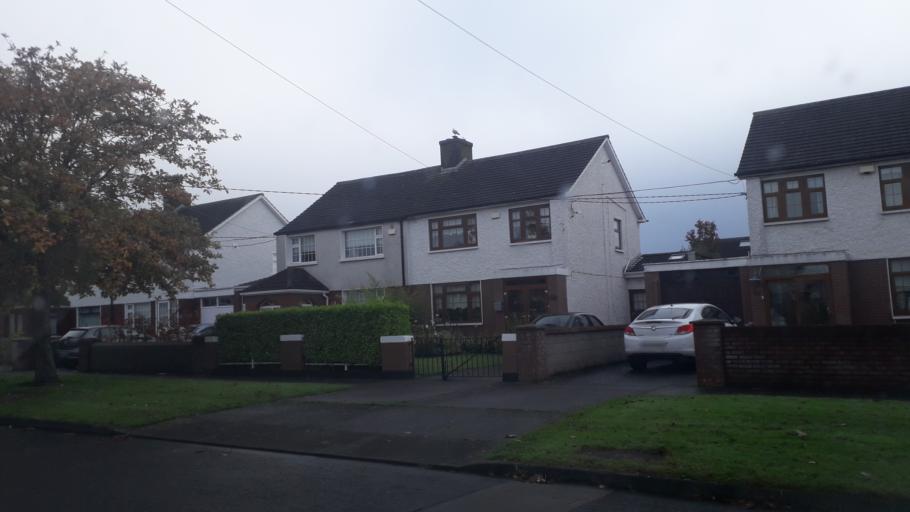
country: IE
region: Leinster
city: Artane
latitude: 53.3909
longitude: -6.2082
